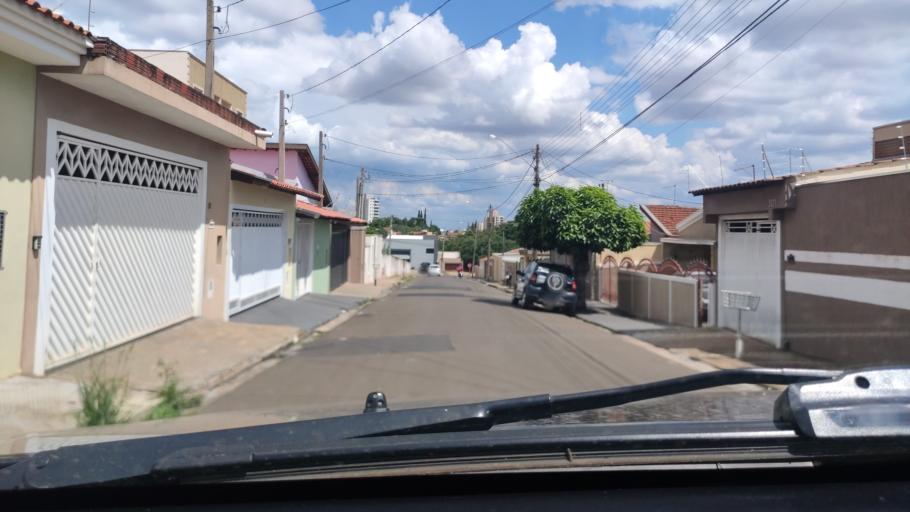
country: BR
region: Sao Paulo
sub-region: Sao Carlos
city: Sao Carlos
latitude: -22.0087
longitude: -47.8729
